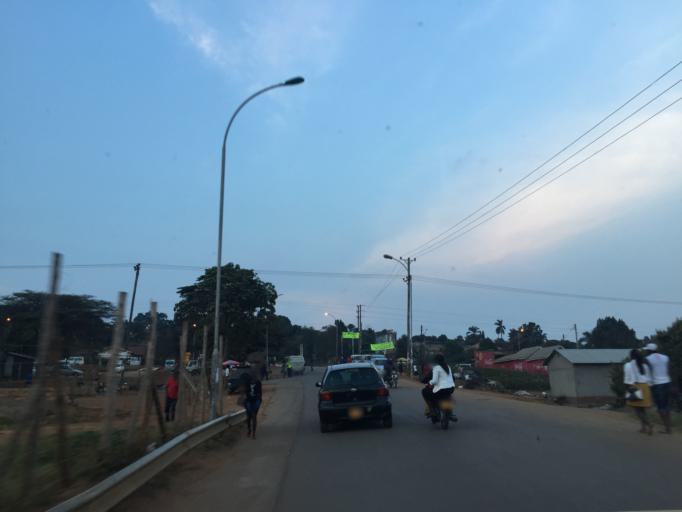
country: UG
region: Central Region
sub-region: Kampala District
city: Kampala
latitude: 0.2572
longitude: 32.6274
